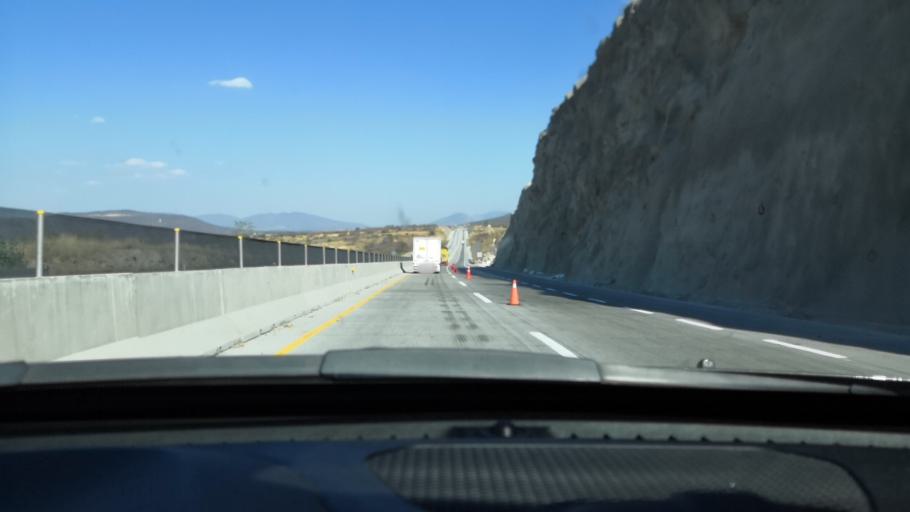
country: MX
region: Jalisco
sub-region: Tlajomulco de Zuniga
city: San Lucas Evangelista
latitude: 20.3917
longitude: -103.3319
